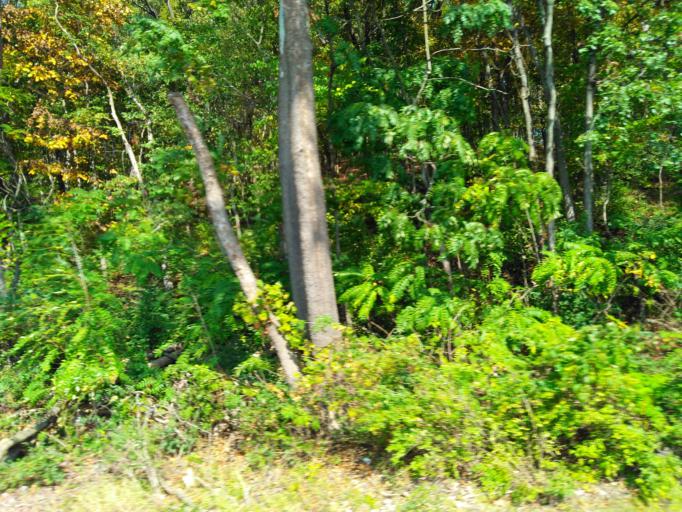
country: US
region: Missouri
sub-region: Saint Louis County
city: Valley Park
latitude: 38.5284
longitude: -90.5364
